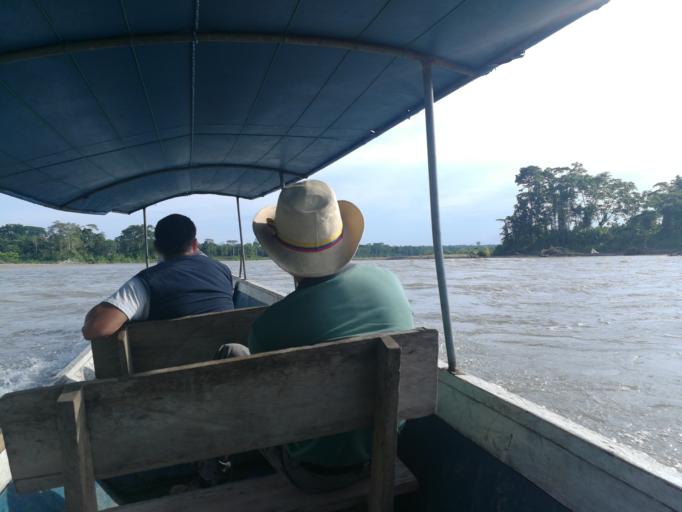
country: EC
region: Orellana
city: Boca Suno
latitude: -0.8326
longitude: -77.1948
